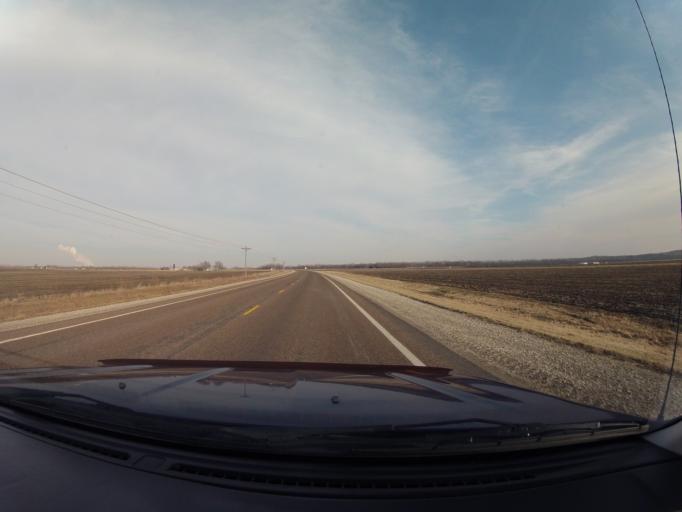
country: US
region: Kansas
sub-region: Pottawatomie County
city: Wamego
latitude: 39.2092
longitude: -96.2662
